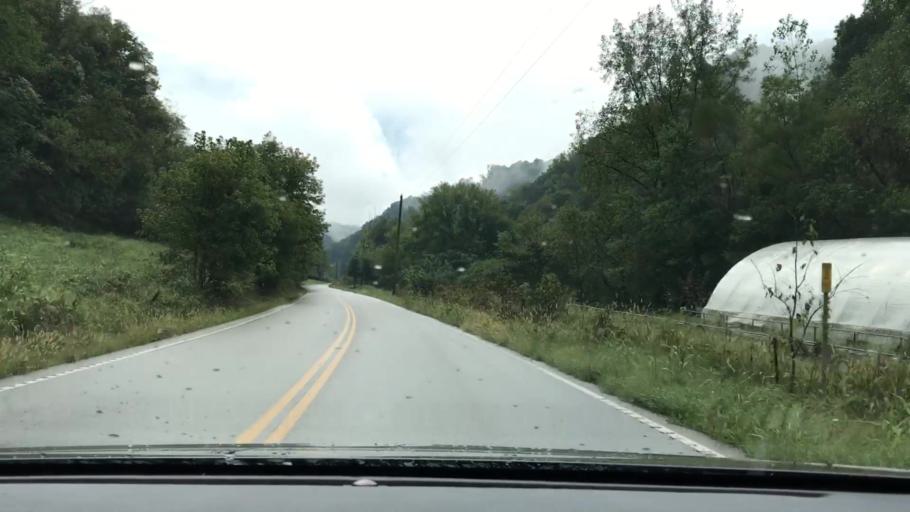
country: US
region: Tennessee
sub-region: Macon County
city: Red Boiling Springs
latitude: 36.4179
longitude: -85.9277
